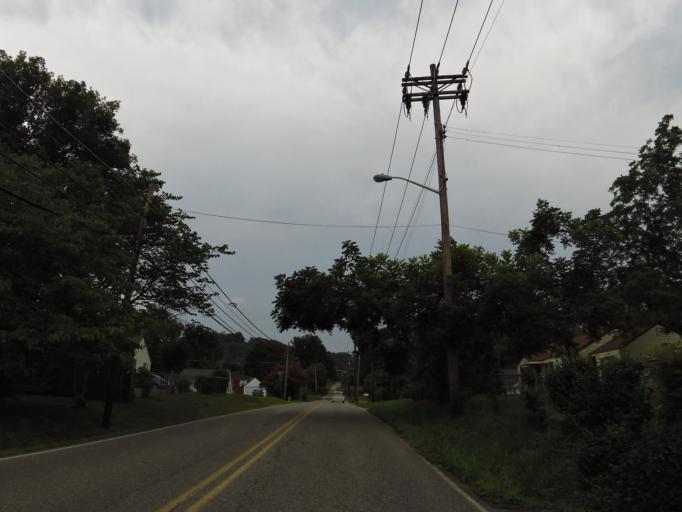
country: US
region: Tennessee
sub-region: Knox County
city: Knoxville
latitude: 35.9445
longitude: -83.8880
